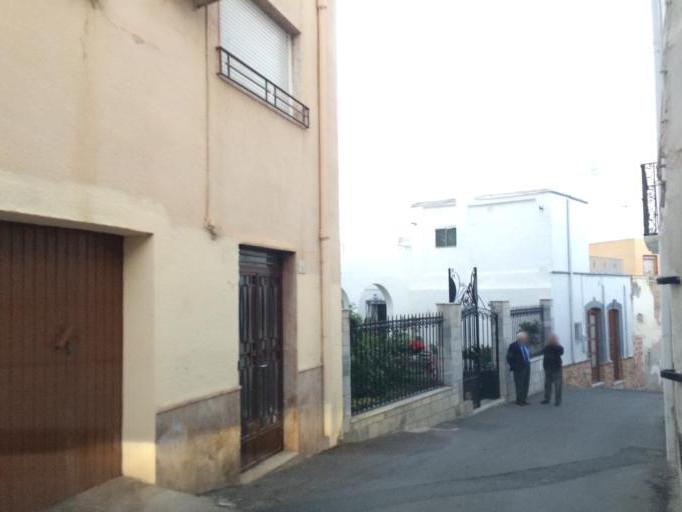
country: ES
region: Andalusia
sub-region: Provincia de Almeria
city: Gador
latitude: 36.9538
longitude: -2.4921
